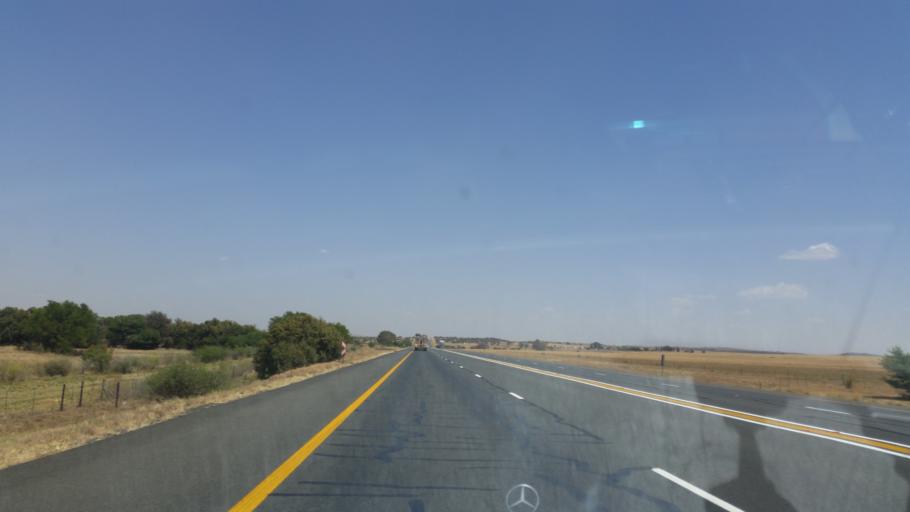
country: ZA
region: Orange Free State
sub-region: Lejweleputswa District Municipality
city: Brandfort
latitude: -28.8946
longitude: 26.4777
